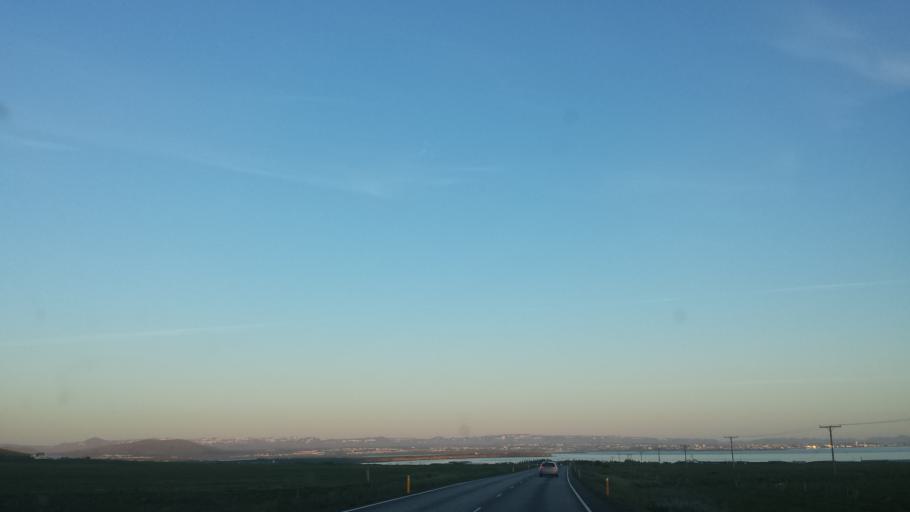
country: IS
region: Capital Region
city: Reykjavik
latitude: 64.2528
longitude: -21.8298
